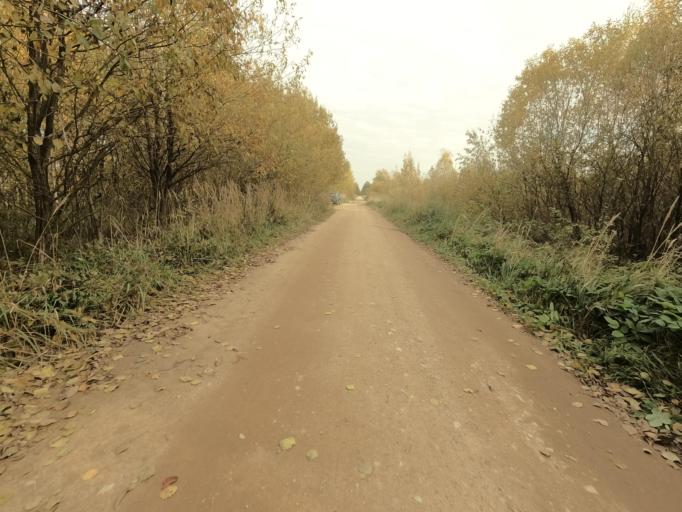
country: RU
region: Novgorod
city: Pankovka
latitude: 58.8968
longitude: 31.0018
